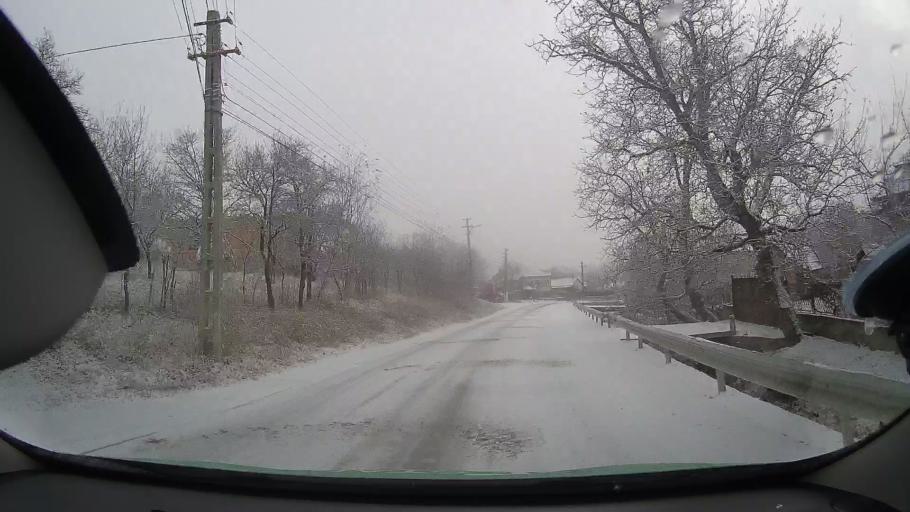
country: RO
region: Alba
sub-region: Comuna Livezile
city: Livezile
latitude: 46.3452
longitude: 23.6547
